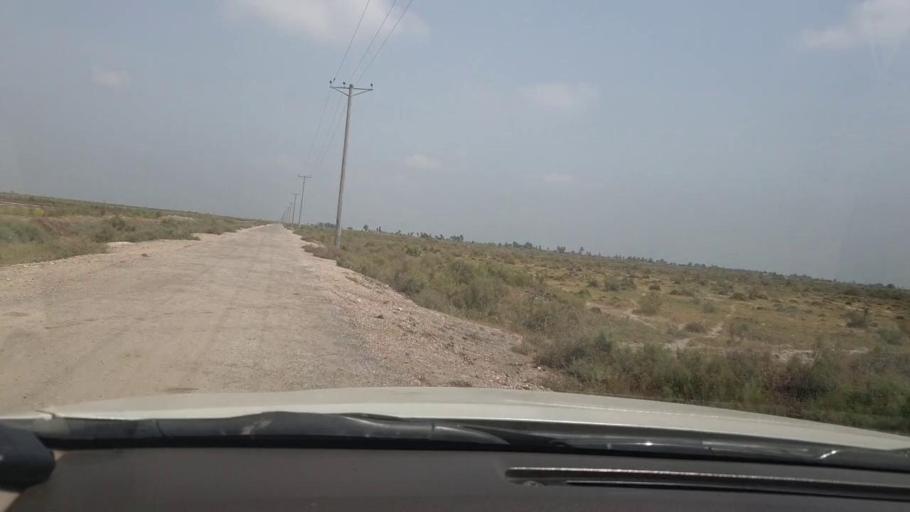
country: PK
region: Sindh
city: Garhi Yasin
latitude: 27.9867
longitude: 68.5019
